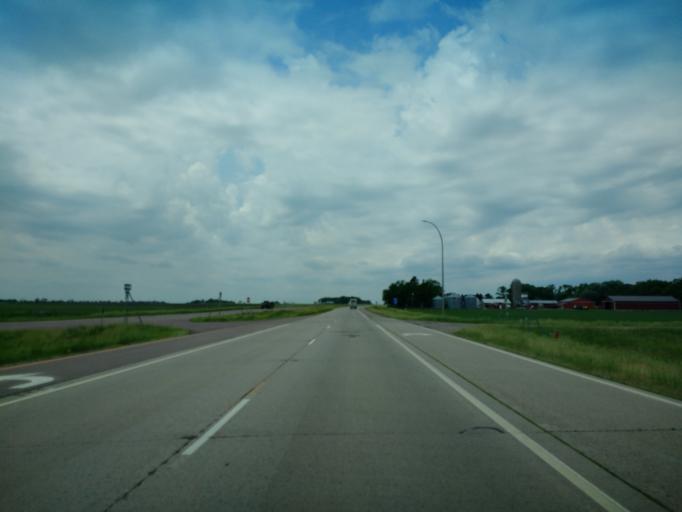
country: US
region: Minnesota
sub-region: Cottonwood County
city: Mountain Lake
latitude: 43.9491
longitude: -94.8186
